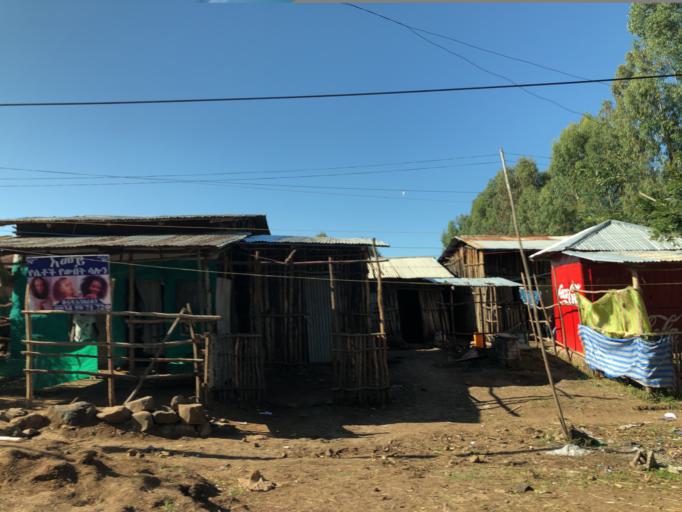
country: ET
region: Amhara
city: Gondar
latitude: 12.4751
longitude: 37.4823
